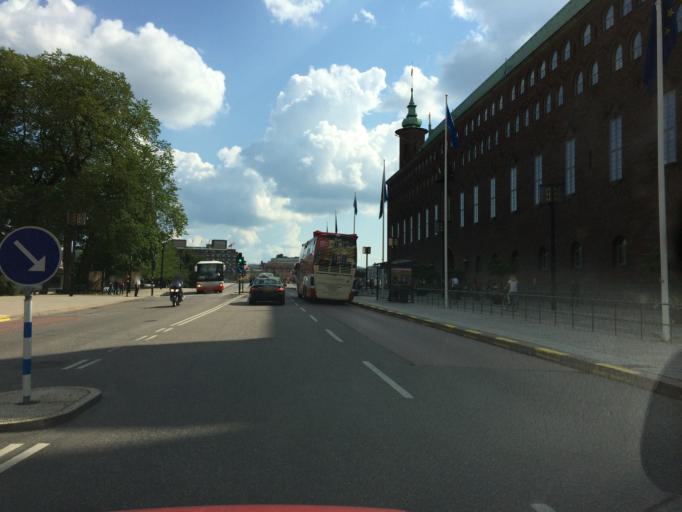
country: SE
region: Stockholm
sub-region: Stockholms Kommun
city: Stockholm
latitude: 59.3279
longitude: 18.0537
